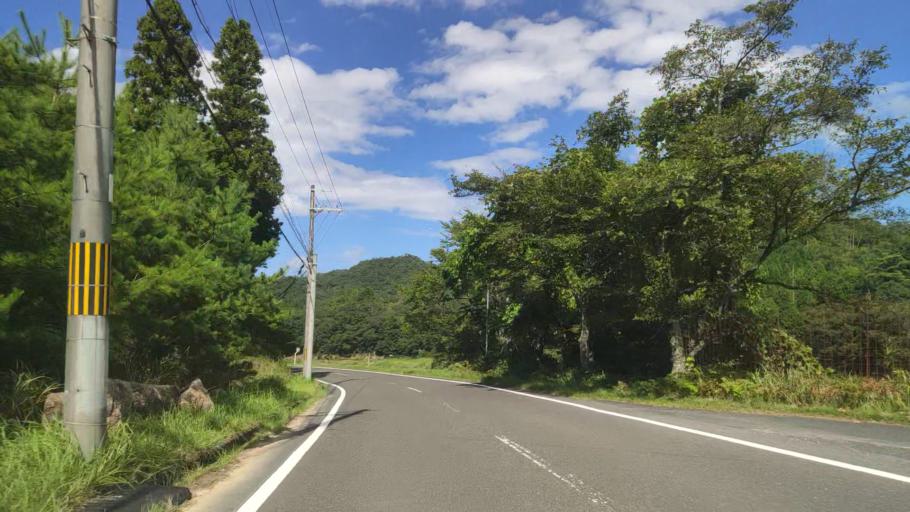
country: JP
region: Hyogo
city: Toyooka
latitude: 35.5563
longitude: 134.9785
